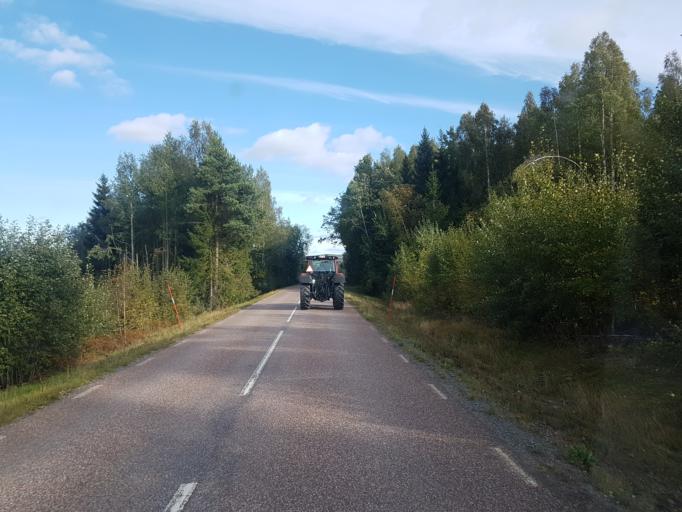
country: SE
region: Dalarna
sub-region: Saters Kommun
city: Saeter
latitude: 60.3666
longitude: 15.7140
